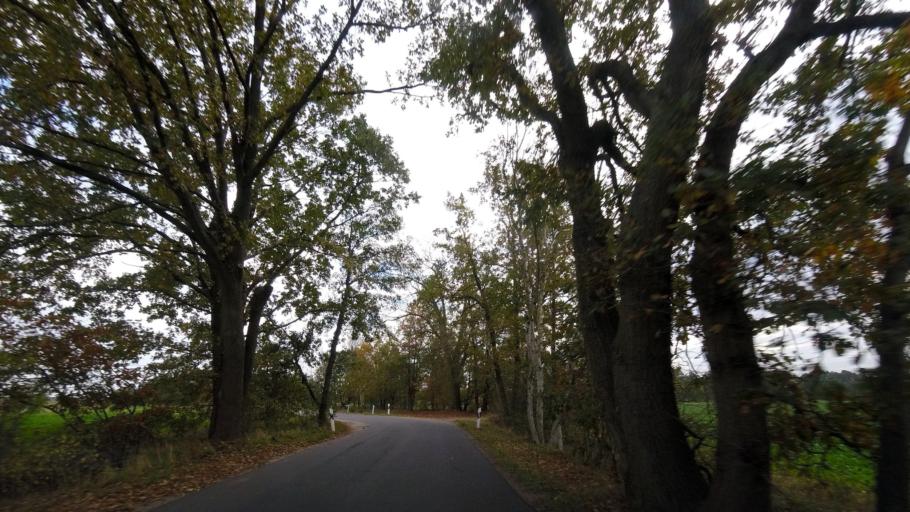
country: DE
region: Brandenburg
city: Borkheide
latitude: 52.1965
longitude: 12.9087
